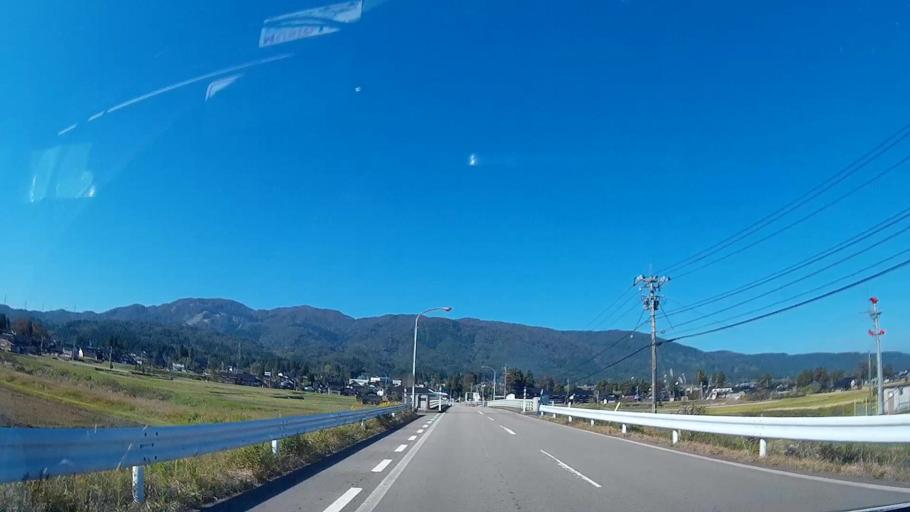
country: JP
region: Toyama
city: Fukumitsu
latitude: 36.5217
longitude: 136.8530
